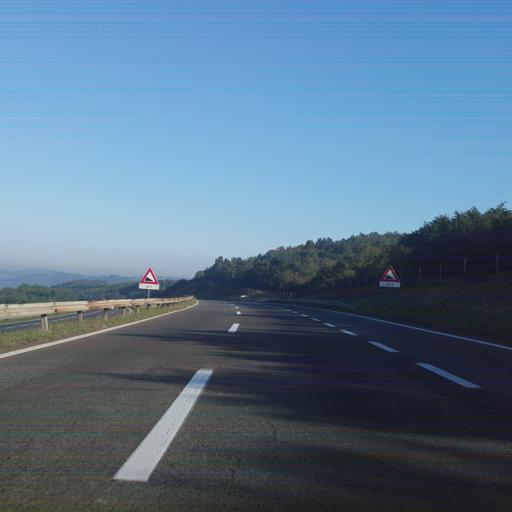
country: RS
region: Central Serbia
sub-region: Belgrade
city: Grocka
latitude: 44.6313
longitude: 20.6379
